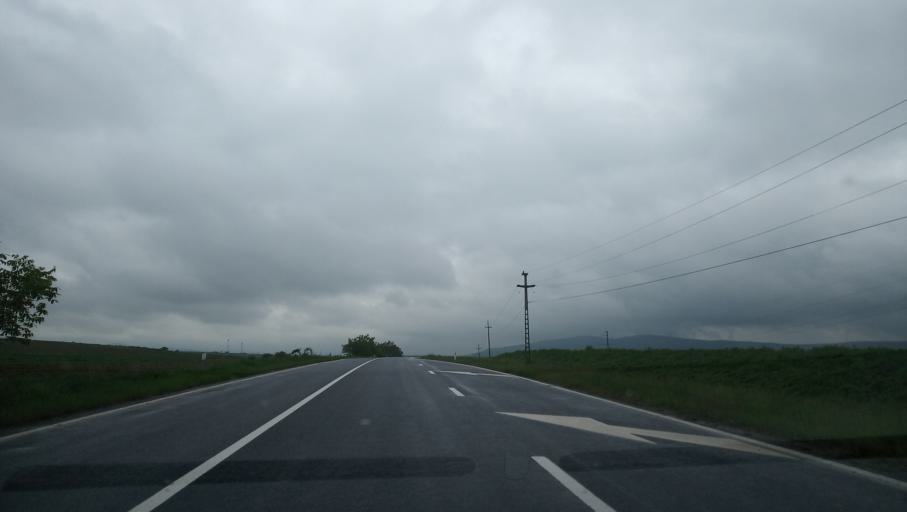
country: RO
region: Alba
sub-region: Comuna Cut
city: Cut
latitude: 45.9183
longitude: 23.7045
